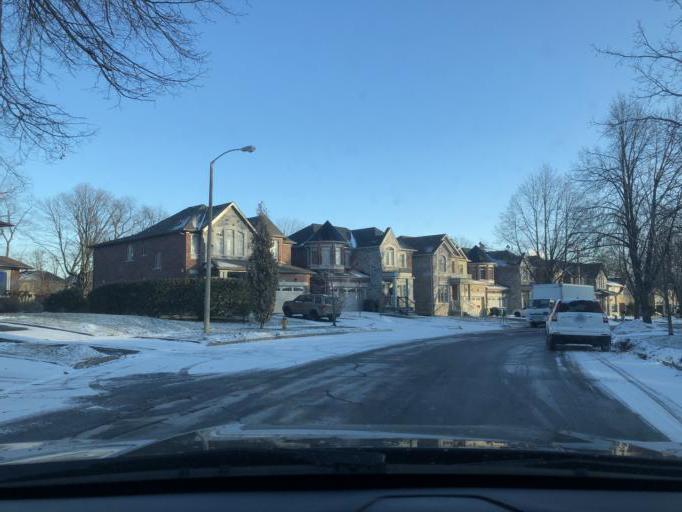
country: CA
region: Ontario
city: Scarborough
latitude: 43.7839
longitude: -79.1519
